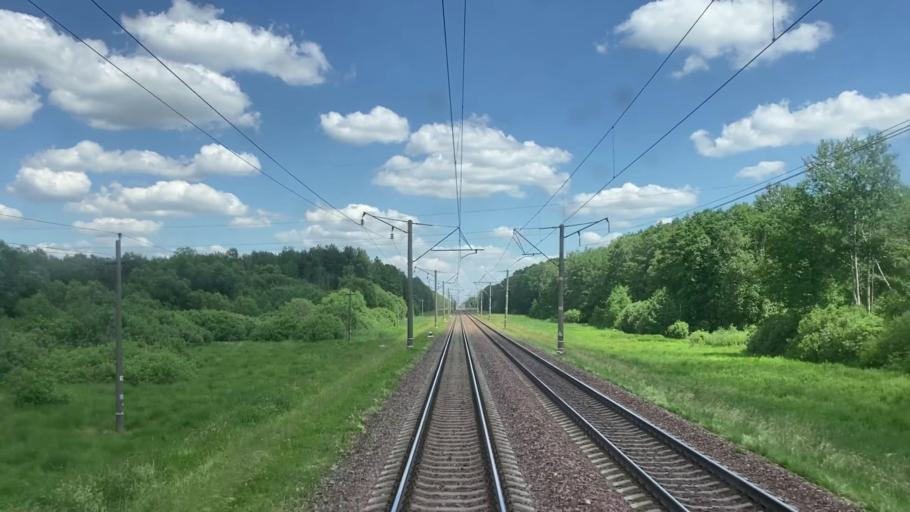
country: BY
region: Brest
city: Pruzhany
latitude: 52.4819
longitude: 24.5598
